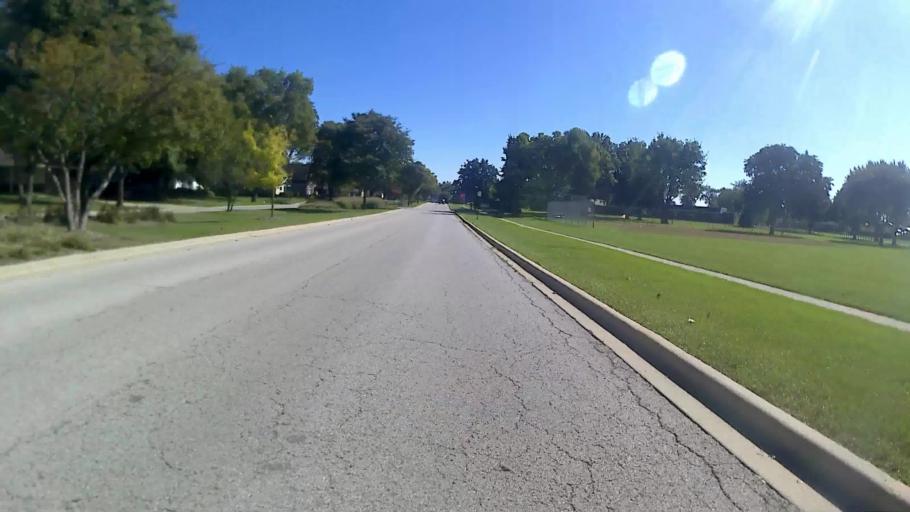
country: US
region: Illinois
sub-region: Cook County
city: Elk Grove Village
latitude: 42.0104
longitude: -87.9953
